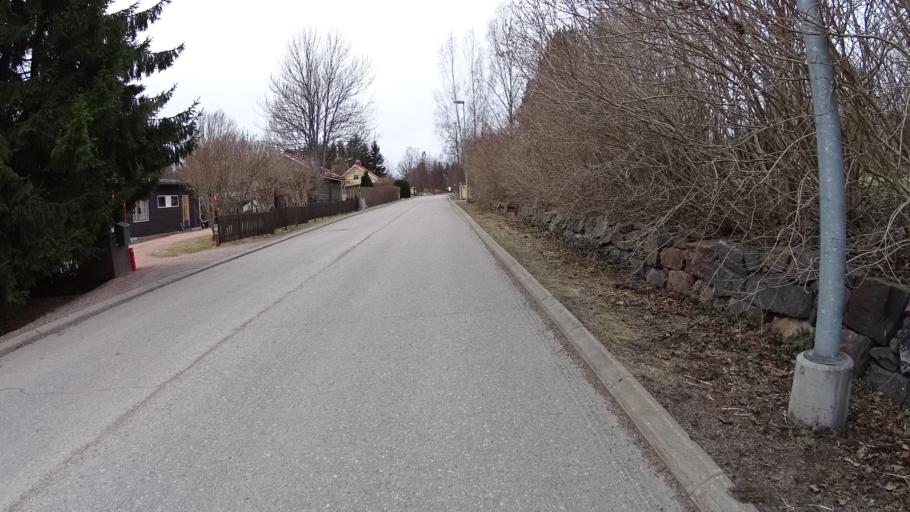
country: FI
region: Uusimaa
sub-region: Helsinki
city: Kauniainen
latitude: 60.2248
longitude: 24.7028
